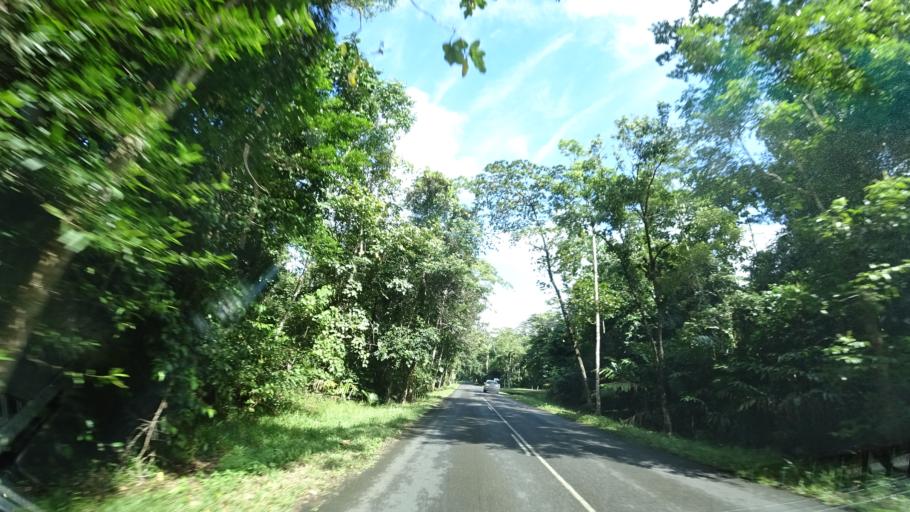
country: AU
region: Queensland
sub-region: Cairns
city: Port Douglas
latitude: -16.2056
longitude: 145.4092
